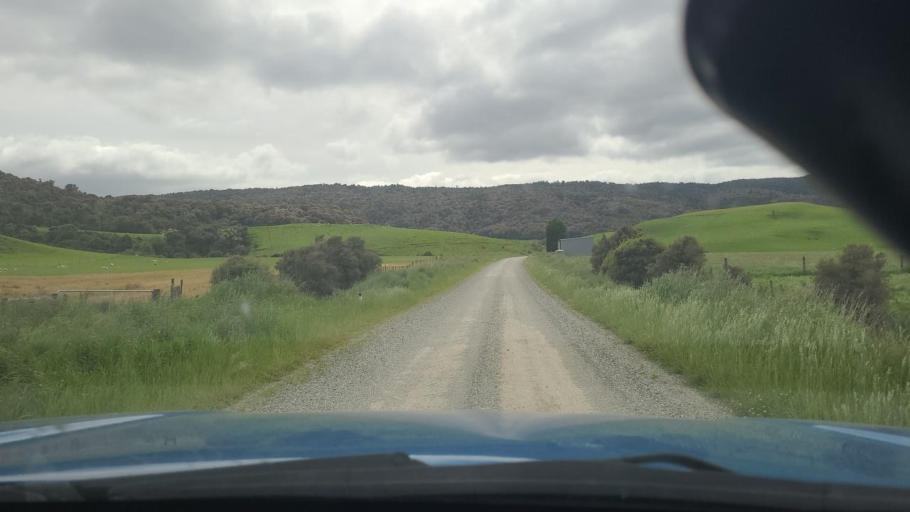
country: NZ
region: Otago
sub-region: Clutha District
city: Papatowai
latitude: -46.5058
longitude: 169.1535
